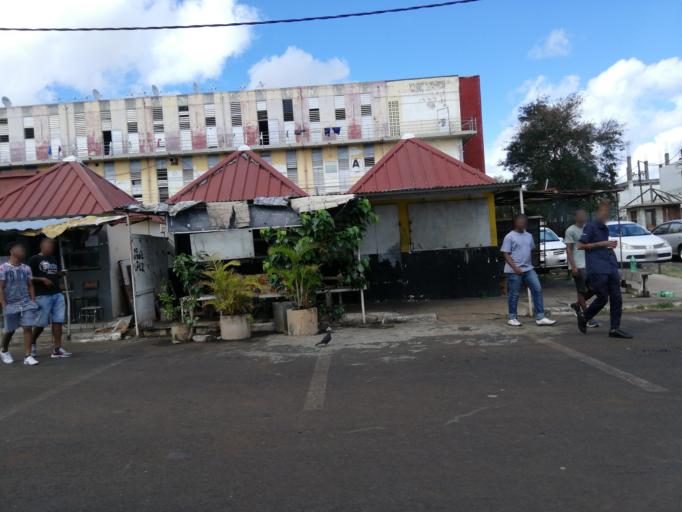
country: MU
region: Black River
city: Petite Riviere
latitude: -20.1909
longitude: 57.4660
